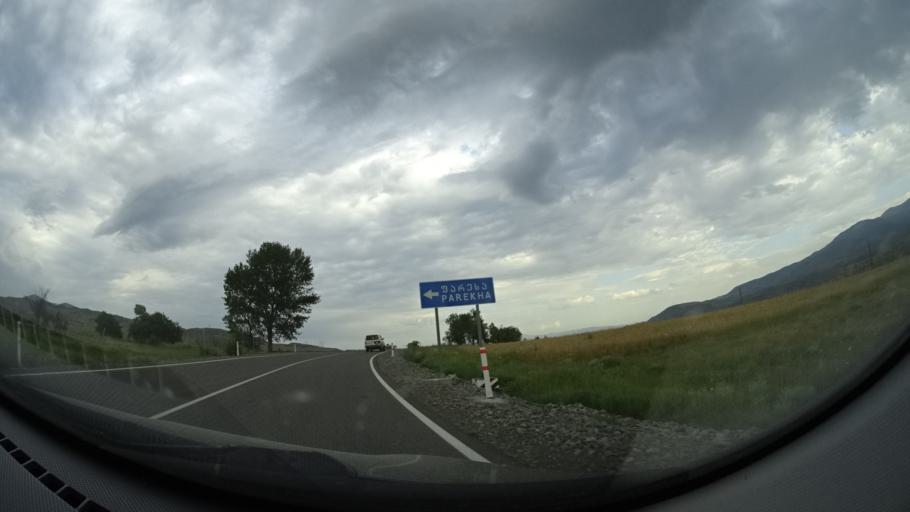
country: GE
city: Vale
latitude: 41.6517
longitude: 42.8795
